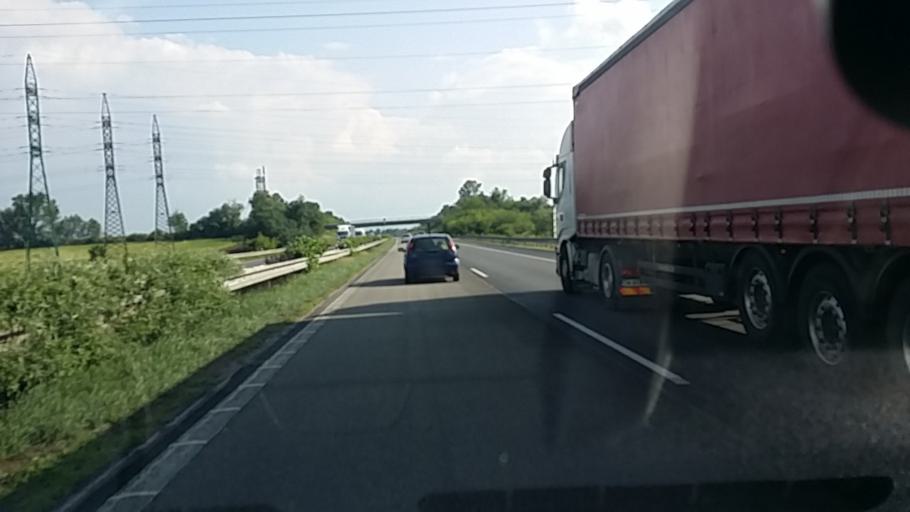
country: SK
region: Bratislavsky
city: Stupava
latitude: 48.2896
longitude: 17.0105
